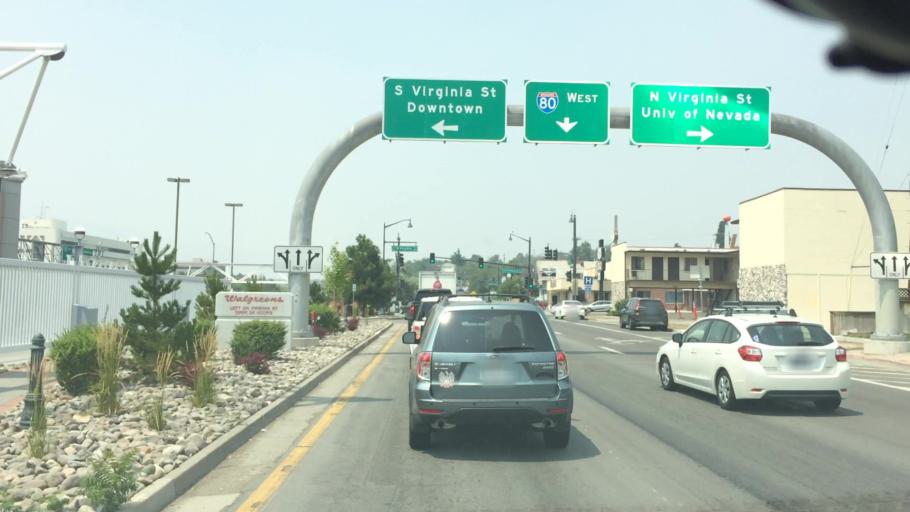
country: US
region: Nevada
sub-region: Washoe County
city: Reno
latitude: 39.5352
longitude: -119.8148
